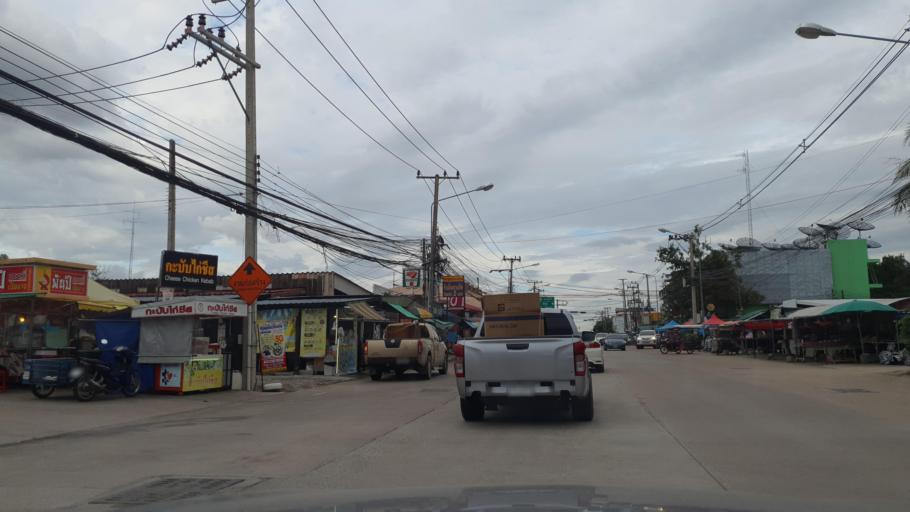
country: TH
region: Chon Buri
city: Phatthaya
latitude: 12.8820
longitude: 100.9026
